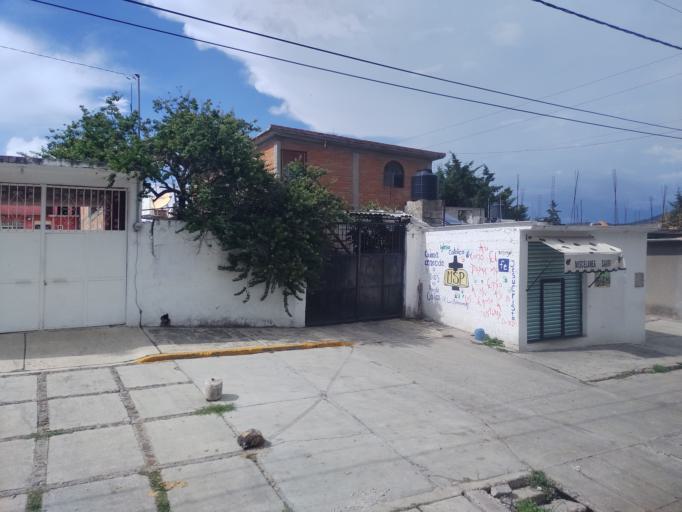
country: MX
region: Mexico
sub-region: Aculco
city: El Colorado
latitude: 20.1043
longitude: -99.7317
